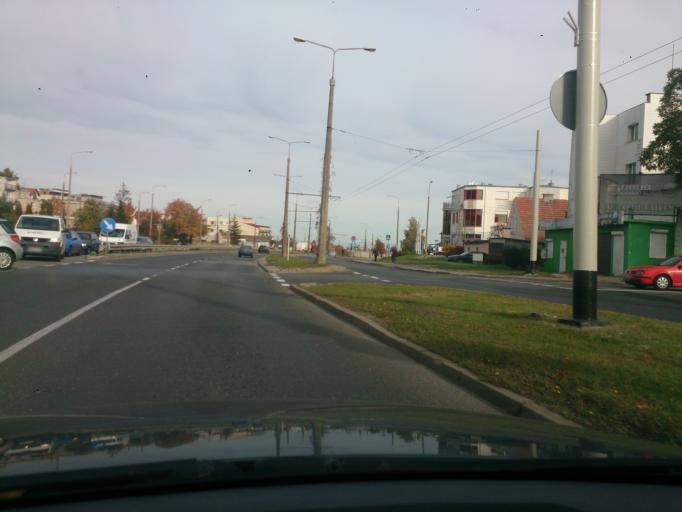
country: PL
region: Pomeranian Voivodeship
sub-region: Gdynia
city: Wielki Kack
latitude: 54.4749
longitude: 18.5158
